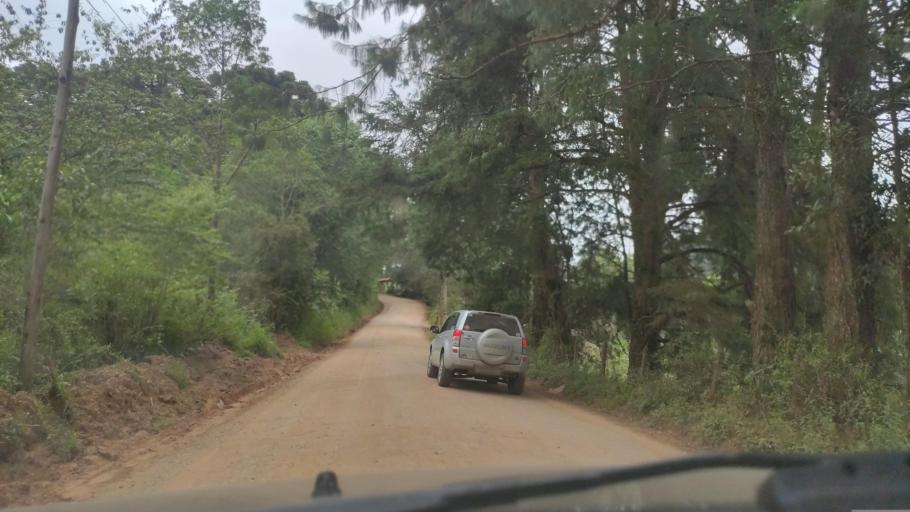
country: BR
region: Minas Gerais
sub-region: Paraisopolis
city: Paraisopolis
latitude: -22.6630
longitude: -45.8680
